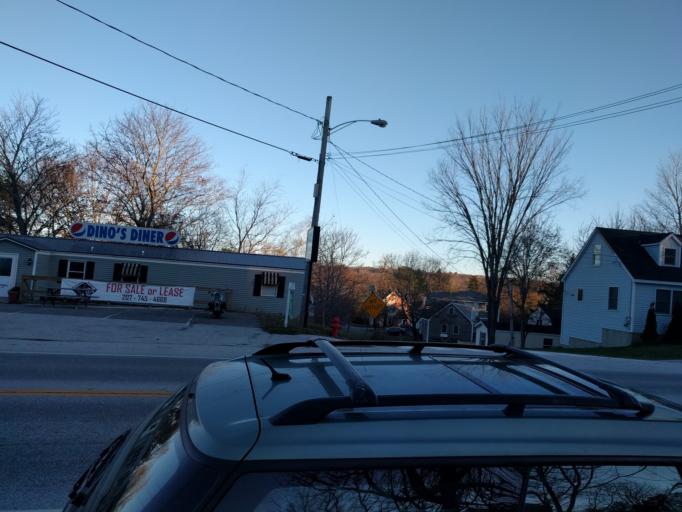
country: US
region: Maine
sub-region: Waldo County
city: Winterport
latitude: 44.6373
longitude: -68.8455
